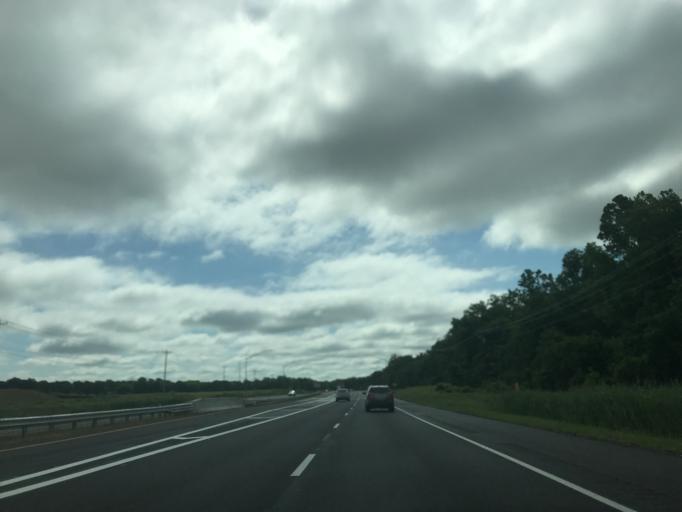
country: US
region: Maryland
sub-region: Caroline County
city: Ridgely
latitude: 38.9259
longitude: -75.9896
